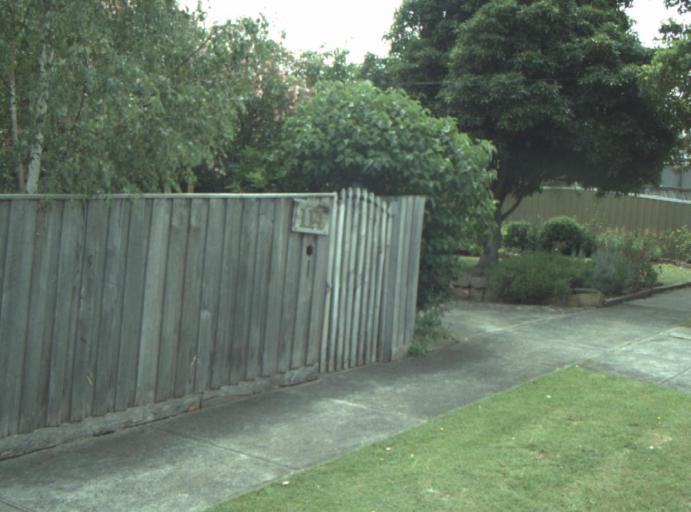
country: AU
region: Victoria
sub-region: Greater Geelong
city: Wandana Heights
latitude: -38.1785
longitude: 144.3240
